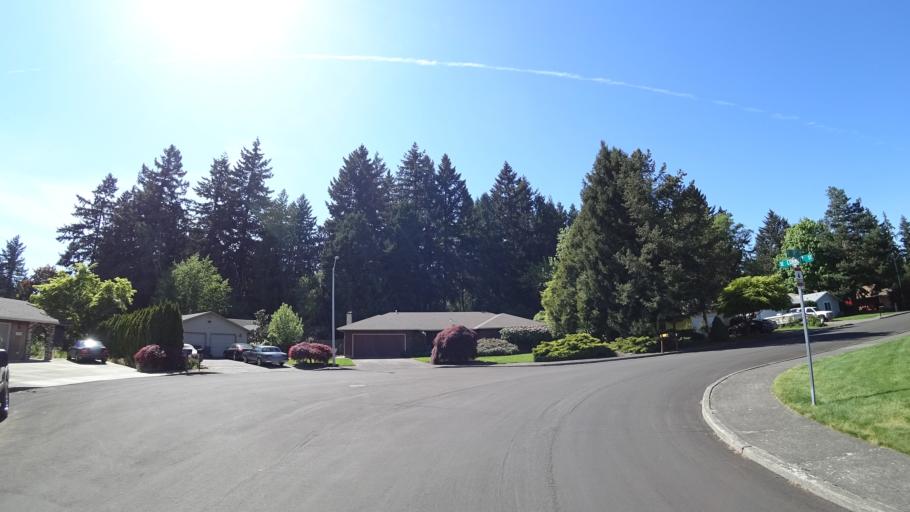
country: US
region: Oregon
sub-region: Washington County
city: Hillsboro
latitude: 45.5157
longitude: -122.9537
